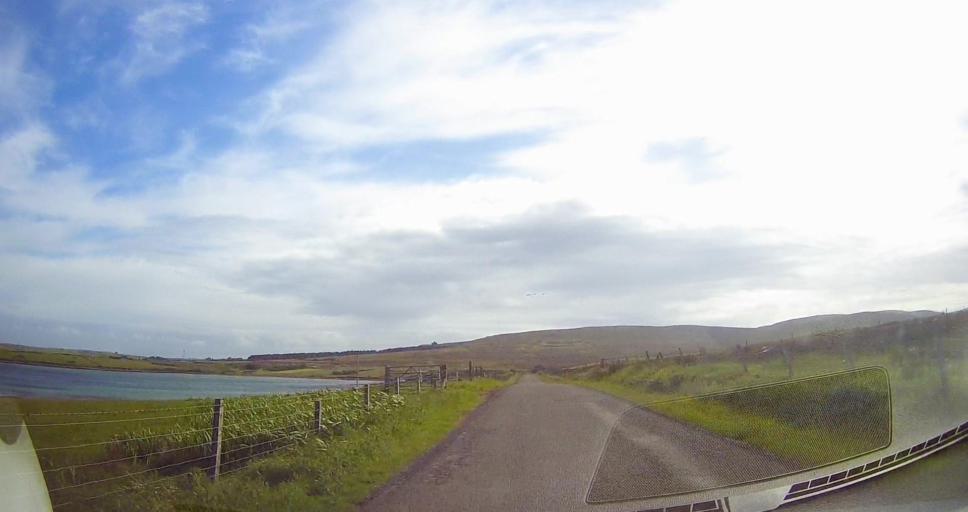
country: GB
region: Scotland
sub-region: Orkney Islands
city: Stromness
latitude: 58.8467
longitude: -3.2060
